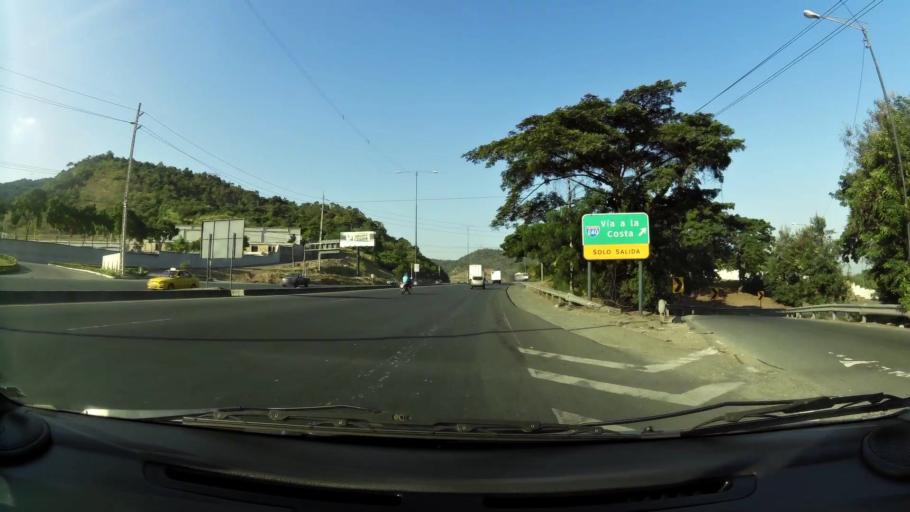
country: EC
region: Guayas
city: Santa Lucia
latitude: -2.1863
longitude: -79.9532
